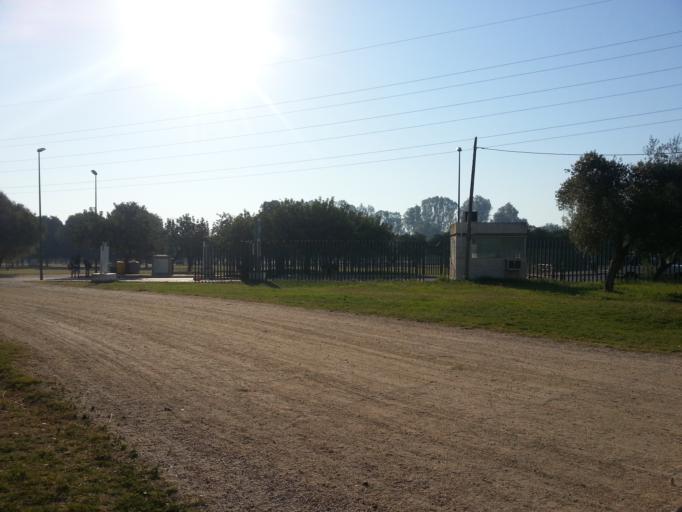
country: ES
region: Andalusia
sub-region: Provincia de Sevilla
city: Sevilla
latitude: 37.4154
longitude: -5.9944
